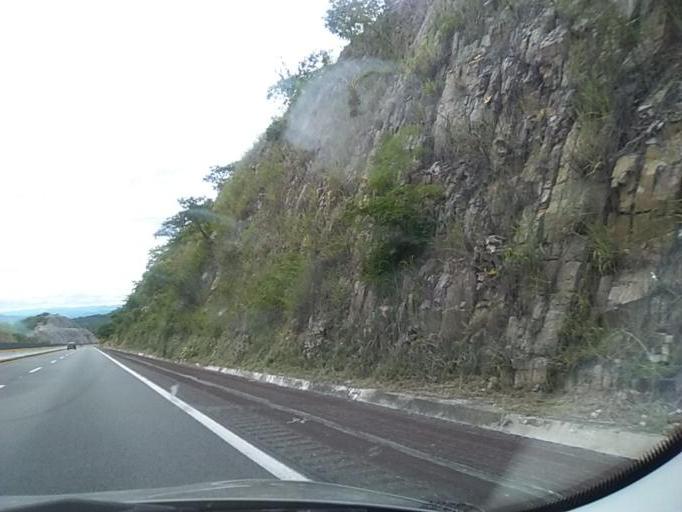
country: MX
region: Guerrero
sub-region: Huitzuco de los Figueroa
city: Ciudad de Huitzuco
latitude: 18.1927
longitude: -99.2056
